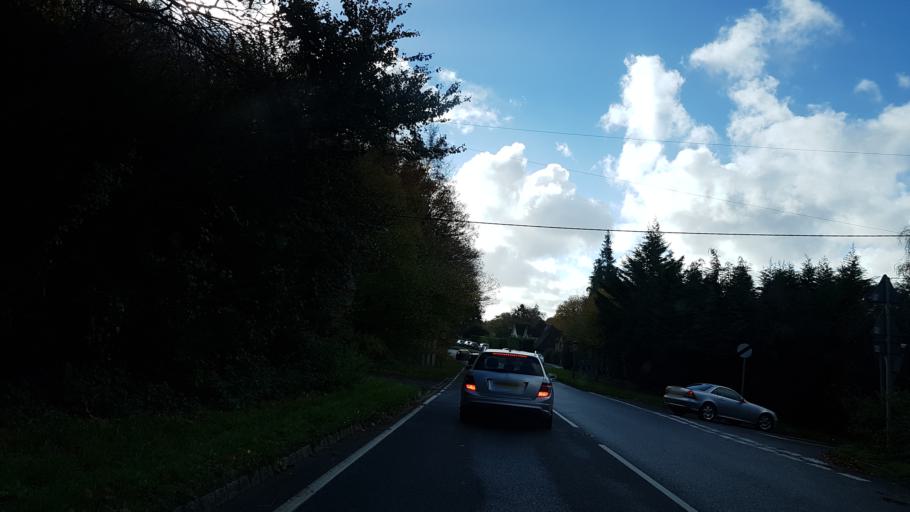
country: GB
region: England
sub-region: Surrey
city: Milford
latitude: 51.1376
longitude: -0.6723
